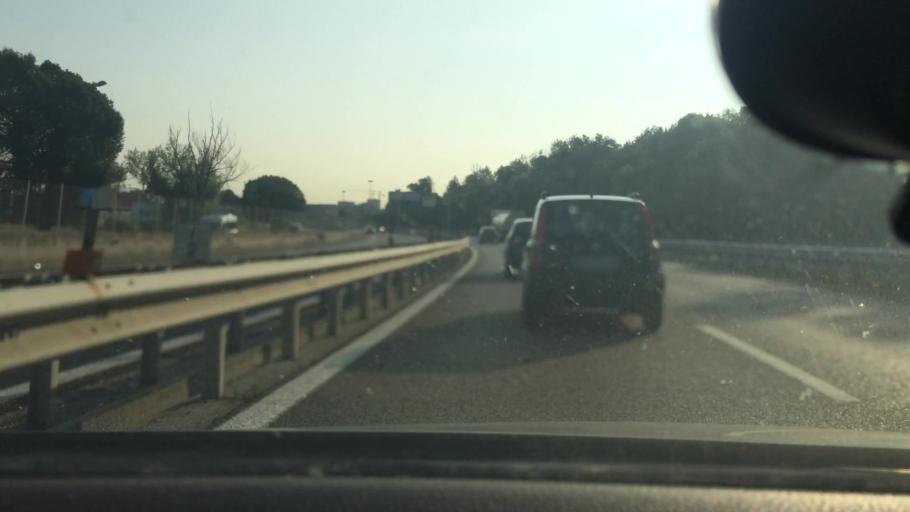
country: IT
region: Lombardy
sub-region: Citta metropolitana di Milano
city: Figino
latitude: 45.4985
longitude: 9.0856
